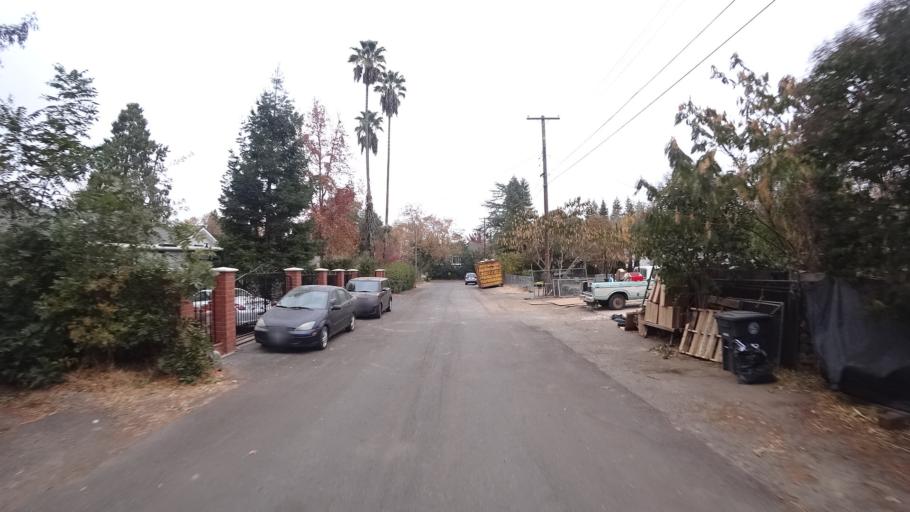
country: US
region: California
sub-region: Sacramento County
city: Citrus Heights
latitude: 38.6988
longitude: -121.2866
